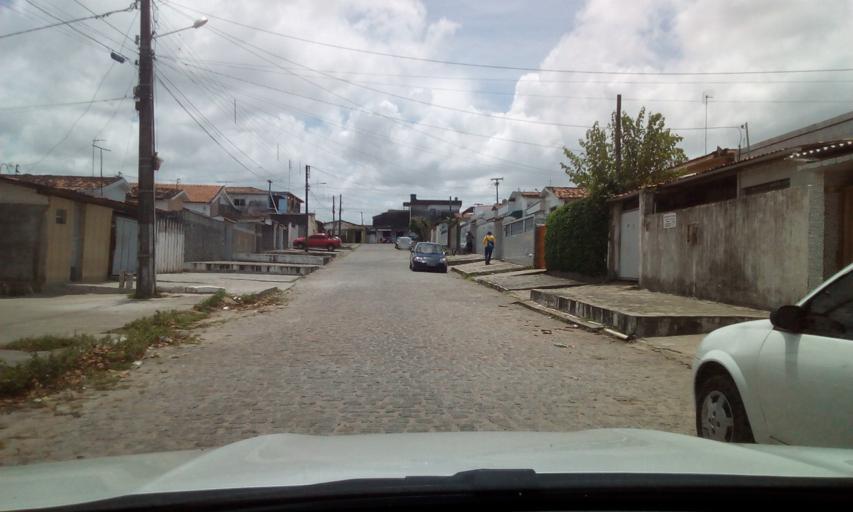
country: BR
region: Paraiba
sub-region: Bayeux
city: Bayeux
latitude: -7.1770
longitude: -34.8933
